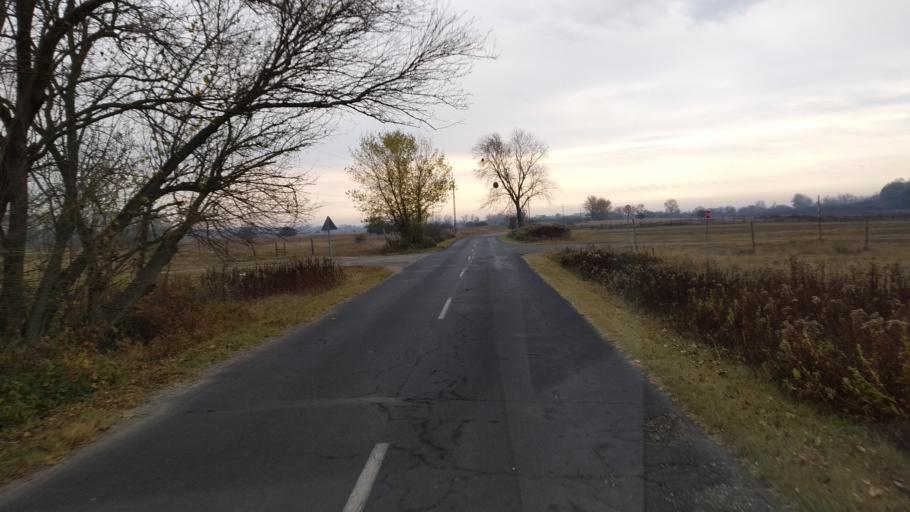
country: HU
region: Pest
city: Tahitotfalu
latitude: 47.7882
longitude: 19.0877
